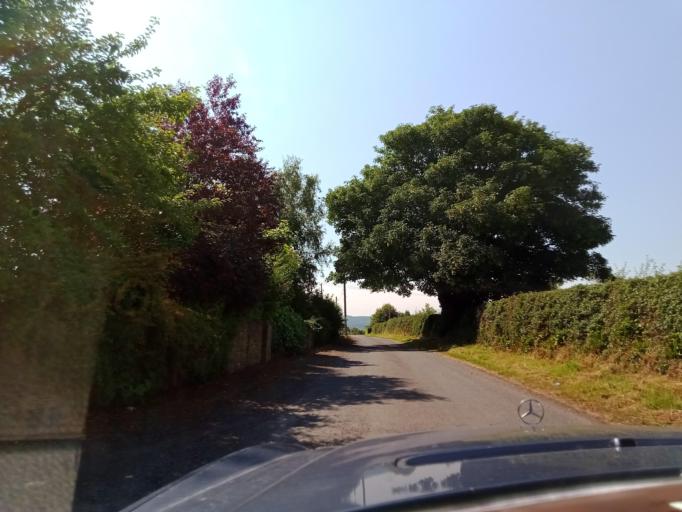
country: IE
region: Leinster
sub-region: Kilkenny
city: Mooncoin
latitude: 52.3102
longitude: -7.2720
